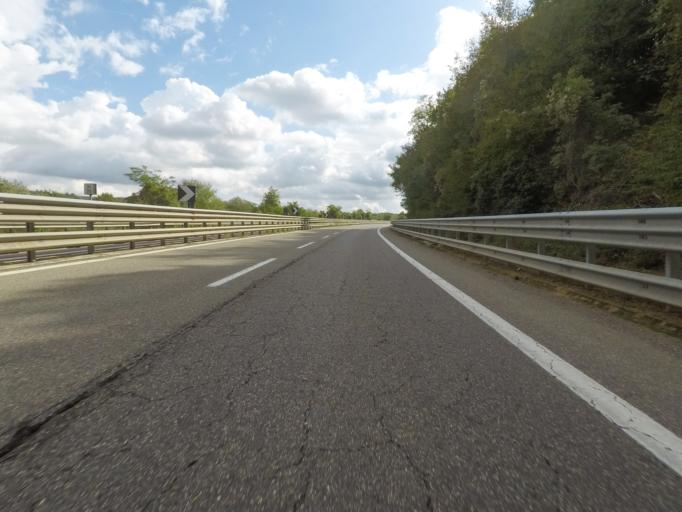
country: IT
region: Tuscany
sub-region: Provincia di Siena
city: Rapolano Terme
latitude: 43.2889
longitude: 11.6207
